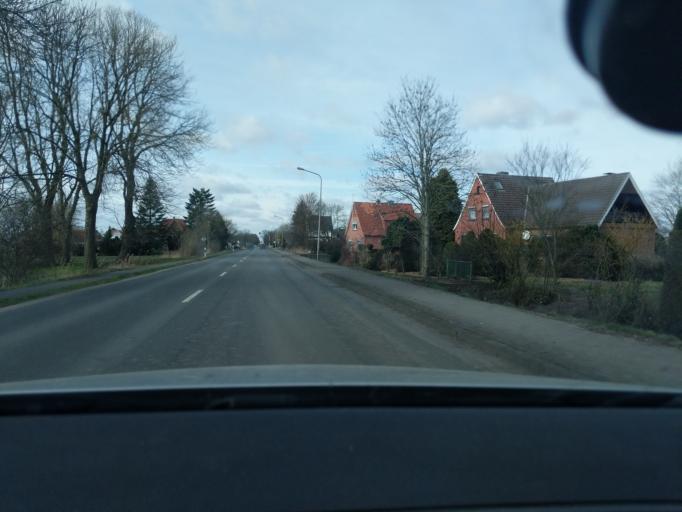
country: DE
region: Lower Saxony
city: Drochtersen
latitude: 53.6983
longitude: 9.4140
